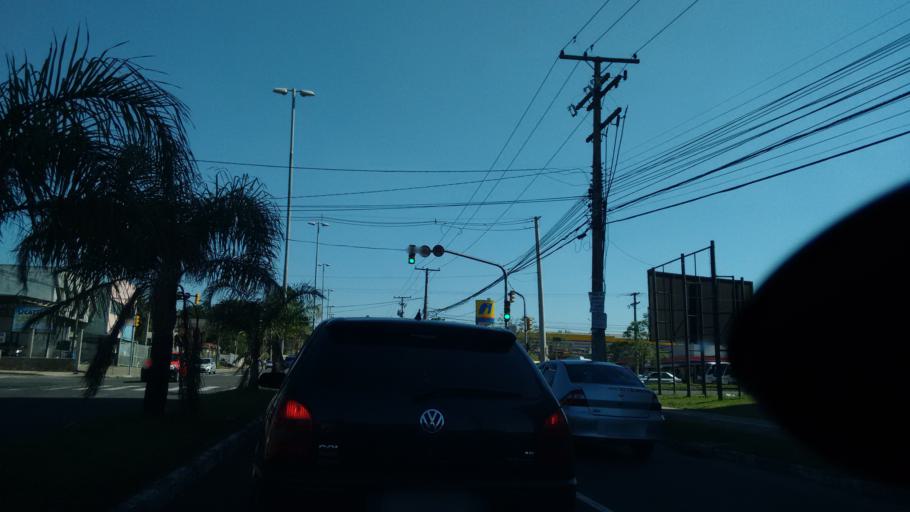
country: BR
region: Rio Grande do Sul
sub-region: Cachoeirinha
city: Cachoeirinha
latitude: -30.0194
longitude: -51.1197
